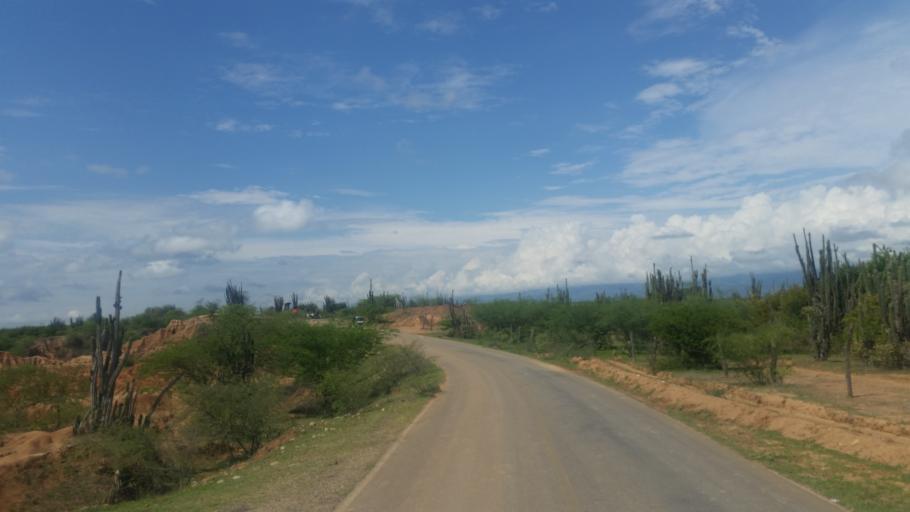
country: CO
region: Huila
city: Villavieja
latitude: 3.2305
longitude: -75.1801
